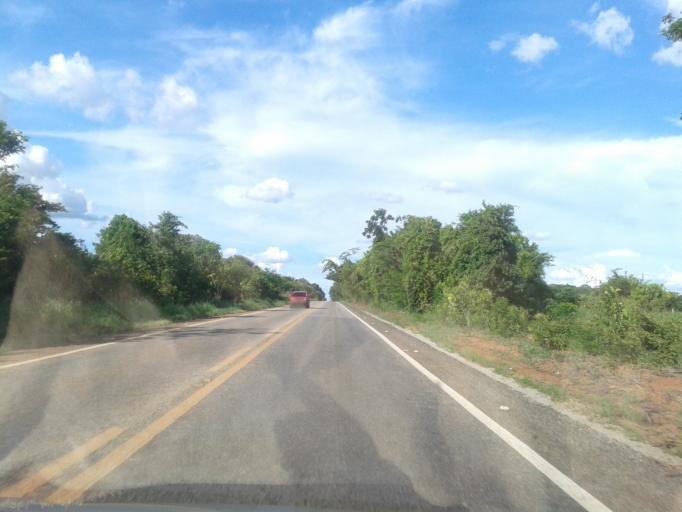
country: BR
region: Goias
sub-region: Mozarlandia
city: Mozarlandia
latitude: -14.4497
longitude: -50.4620
